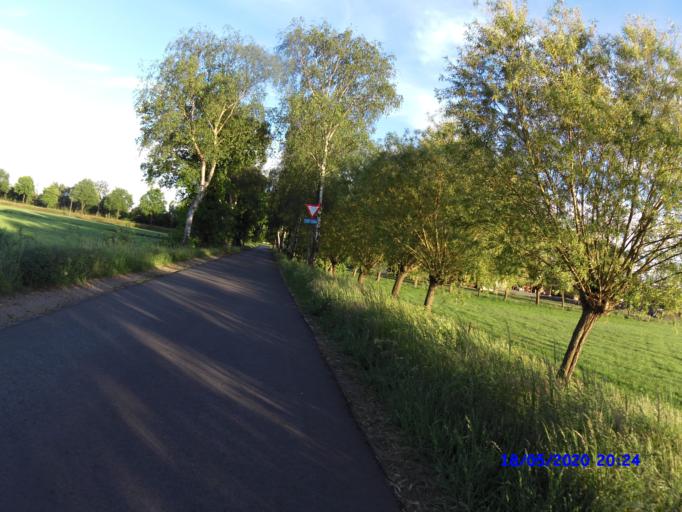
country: BE
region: Flanders
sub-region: Provincie Antwerpen
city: Kasterlee
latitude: 51.2008
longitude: 4.9306
